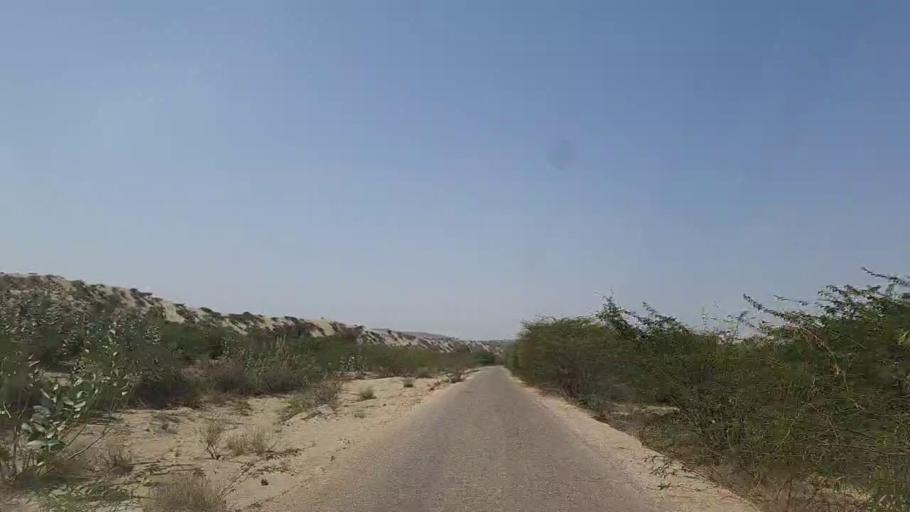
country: PK
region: Sindh
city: Diplo
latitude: 24.5296
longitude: 69.3783
